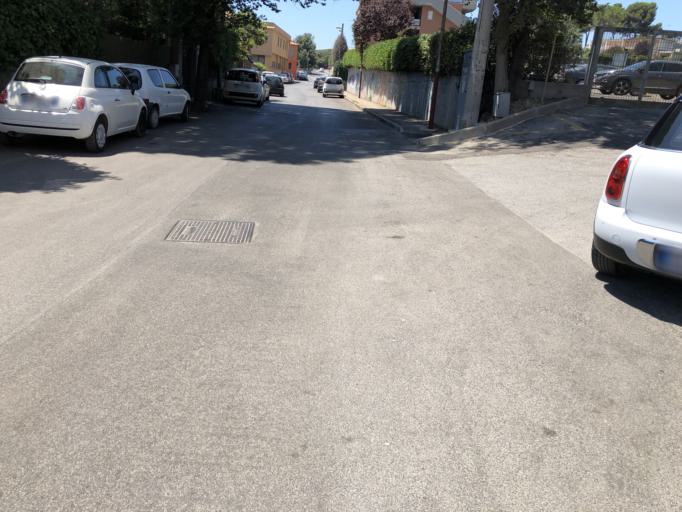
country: IT
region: Latium
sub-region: Citta metropolitana di Roma Capitale
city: Nettuno
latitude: 41.4576
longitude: 12.6515
